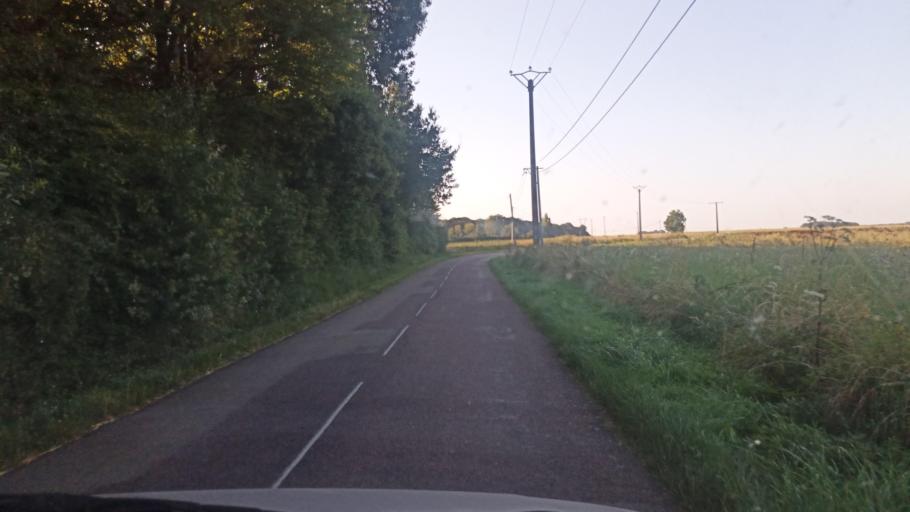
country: FR
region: Bourgogne
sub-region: Departement de l'Yonne
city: Saint-Valerien
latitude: 48.2238
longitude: 3.1198
